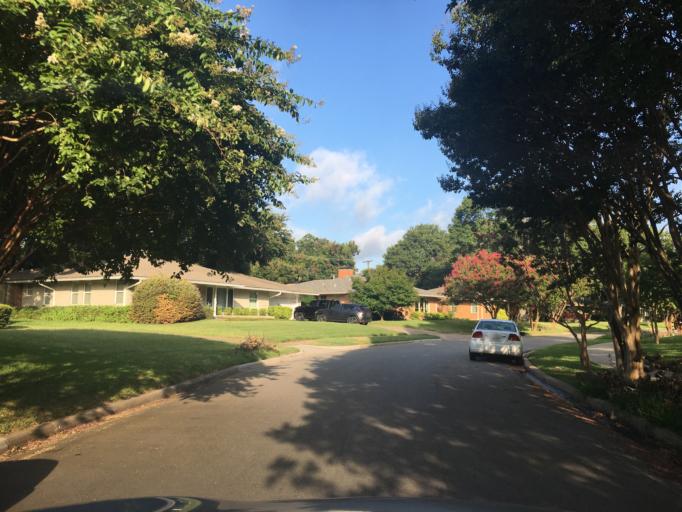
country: US
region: Texas
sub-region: Dallas County
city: Highland Park
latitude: 32.8471
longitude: -96.7507
